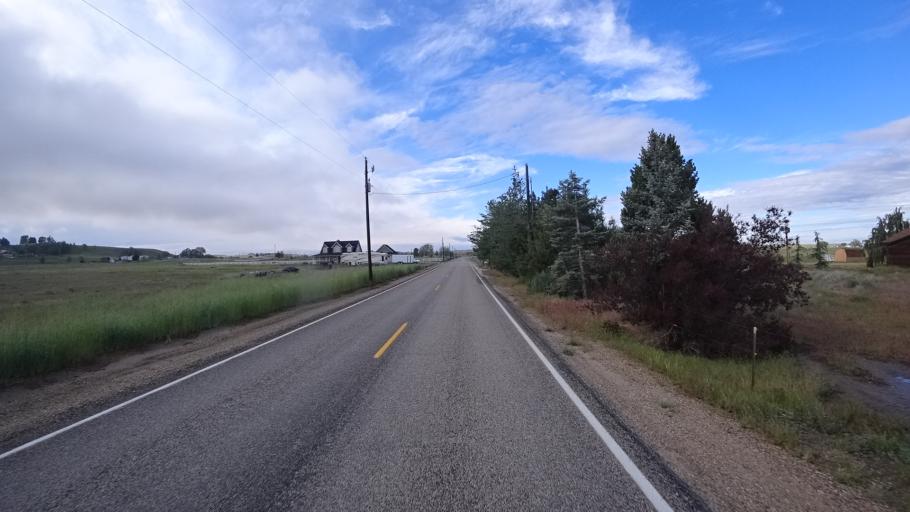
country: US
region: Idaho
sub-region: Ada County
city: Star
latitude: 43.7761
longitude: -116.4731
